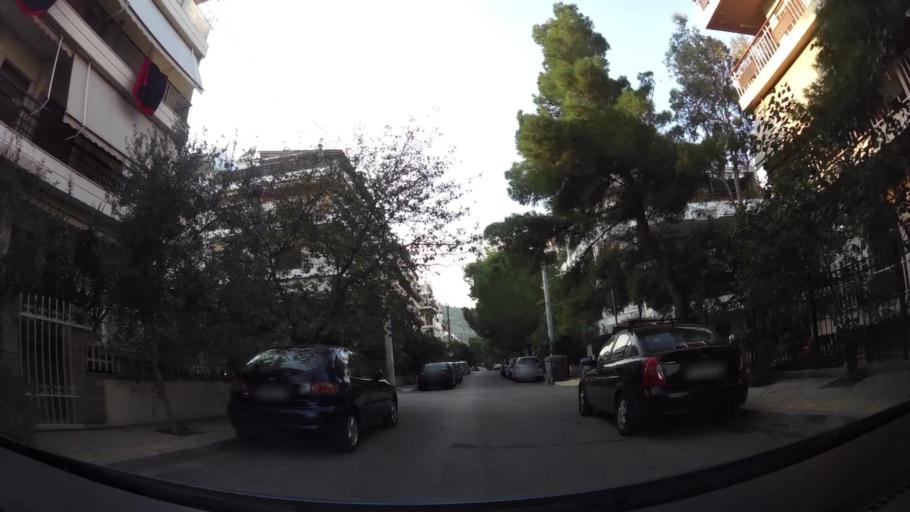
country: GR
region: Attica
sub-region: Nomarchia Athinas
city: Petroupolis
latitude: 38.0354
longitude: 23.6705
